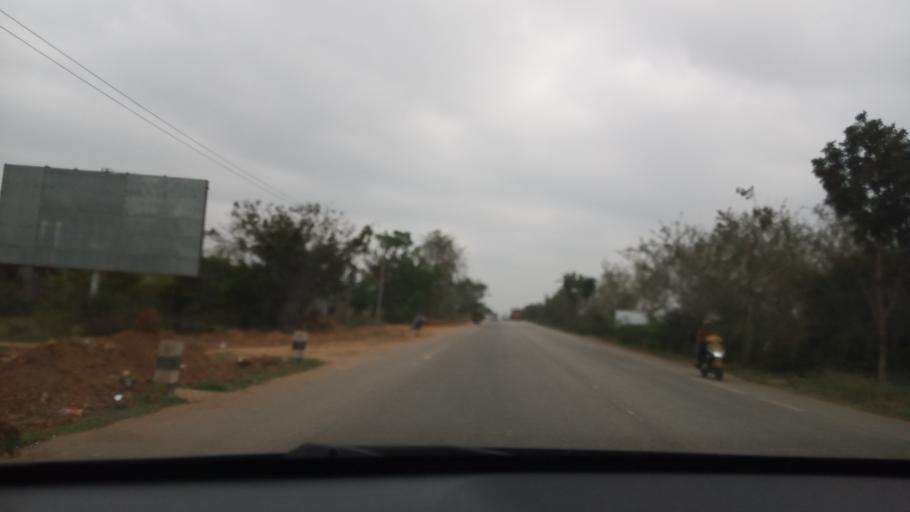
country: IN
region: Karnataka
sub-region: Chikkaballapur
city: Sidlaghatta
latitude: 13.2688
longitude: 77.9484
